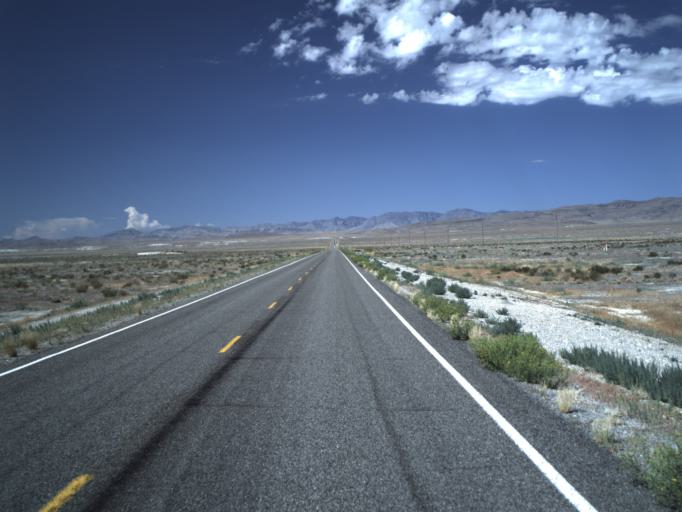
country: US
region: Utah
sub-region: Millard County
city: Delta
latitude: 39.0913
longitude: -113.1708
